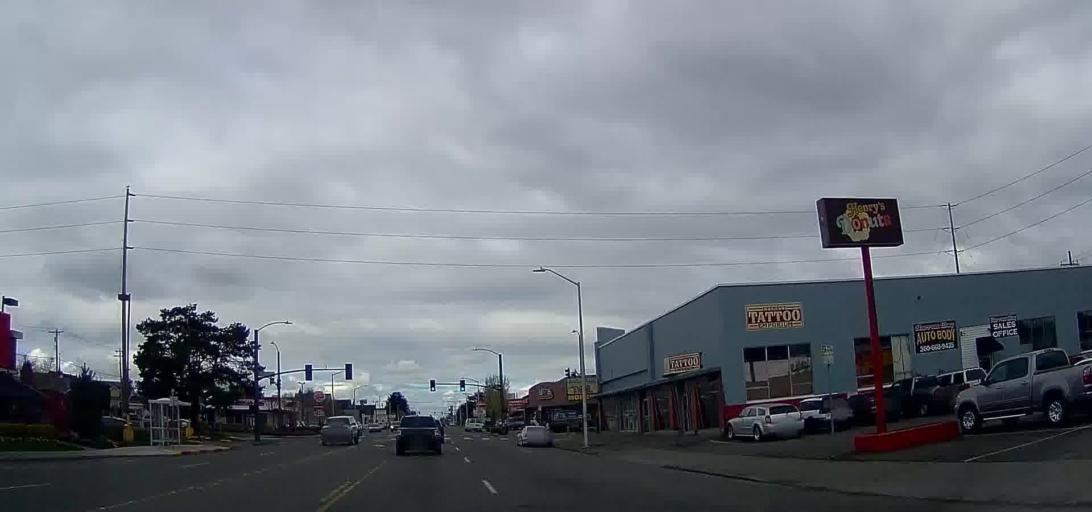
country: US
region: Washington
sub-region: Snohomish County
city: Everett
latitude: 47.9837
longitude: -122.2015
